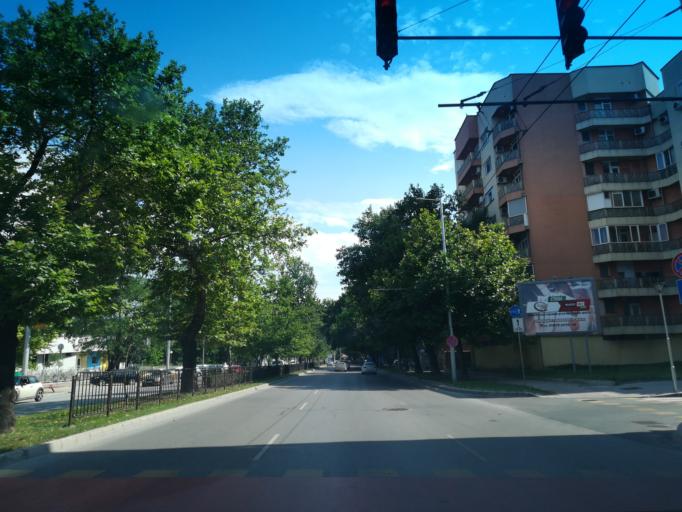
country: BG
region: Plovdiv
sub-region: Obshtina Plovdiv
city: Plovdiv
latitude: 42.1388
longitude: 24.7630
